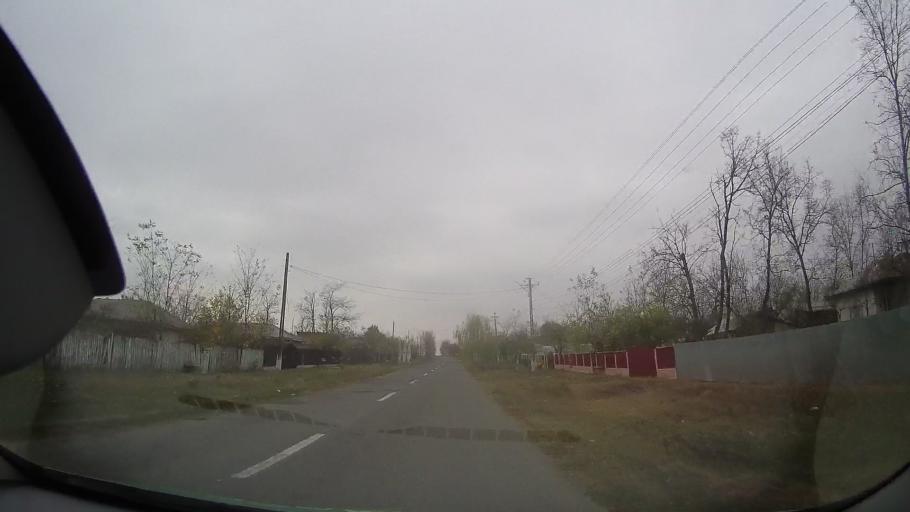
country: RO
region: Ialomita
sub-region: Comuna Grindu
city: Grindu
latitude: 44.7699
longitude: 26.8969
